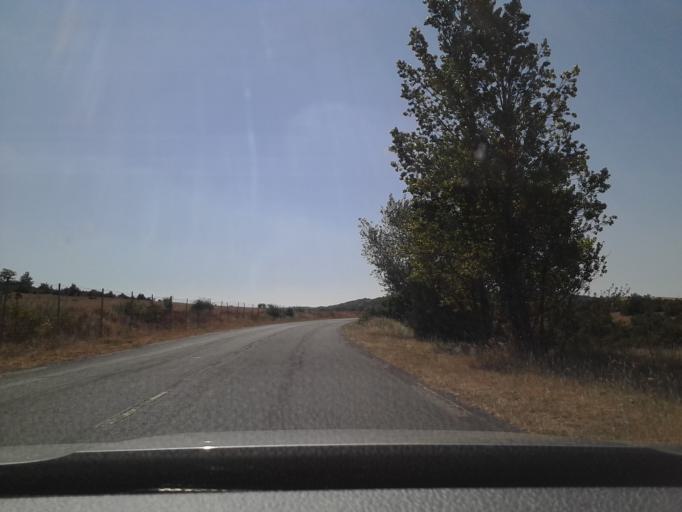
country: FR
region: Midi-Pyrenees
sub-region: Departement de l'Aveyron
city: La Cavalerie
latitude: 43.9200
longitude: 3.2478
